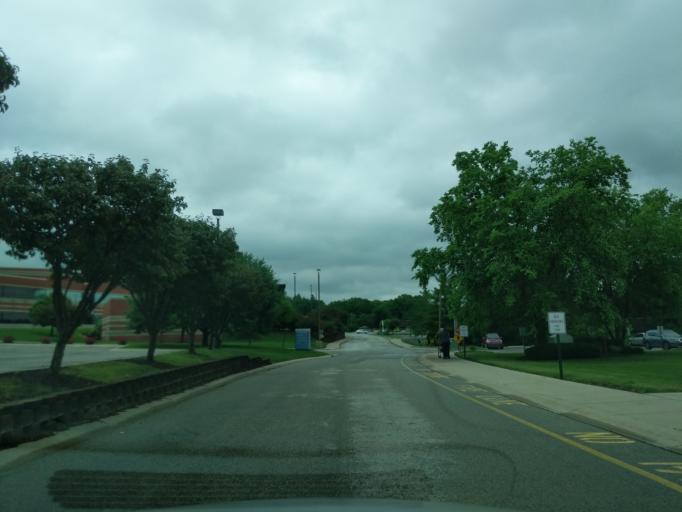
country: US
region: Indiana
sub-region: Hamilton County
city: Noblesville
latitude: 40.0452
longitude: -86.0220
